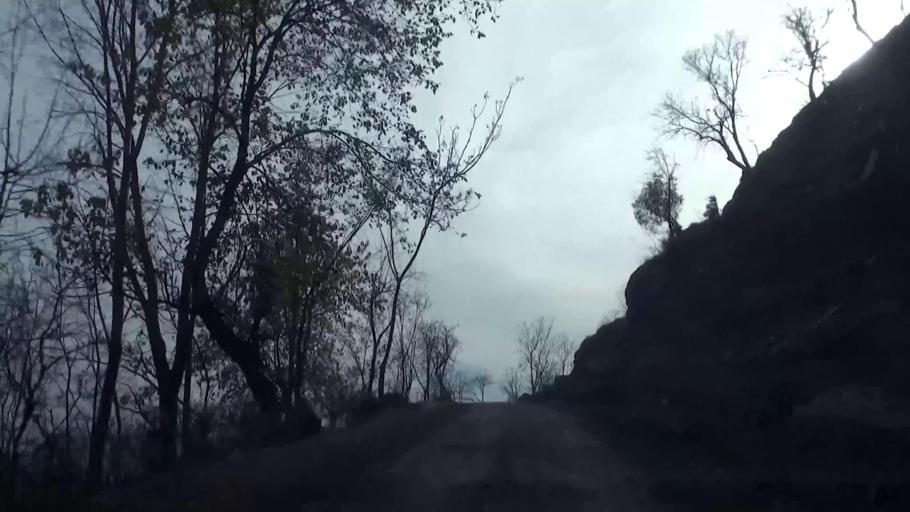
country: PK
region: Azad Kashmir
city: Muzaffarabad
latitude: 34.3661
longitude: 73.5269
